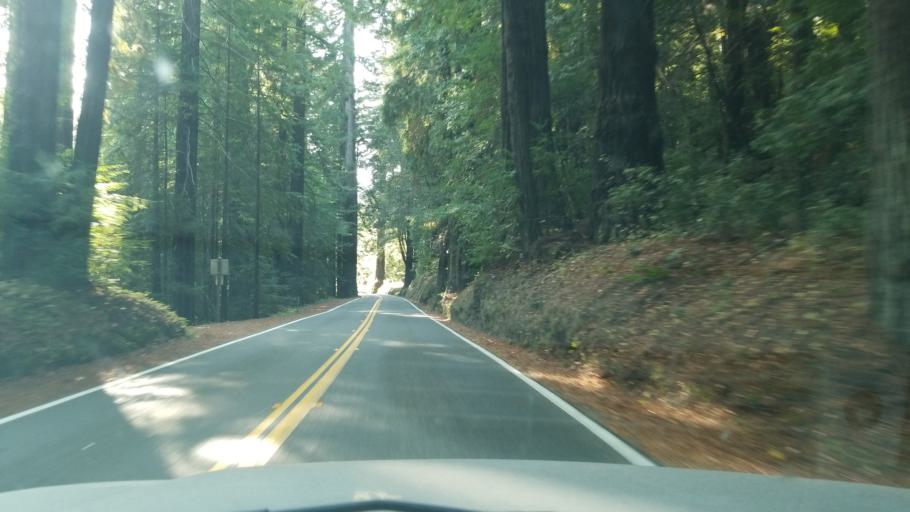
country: US
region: California
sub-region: Humboldt County
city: Redway
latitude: 40.2572
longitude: -123.8266
